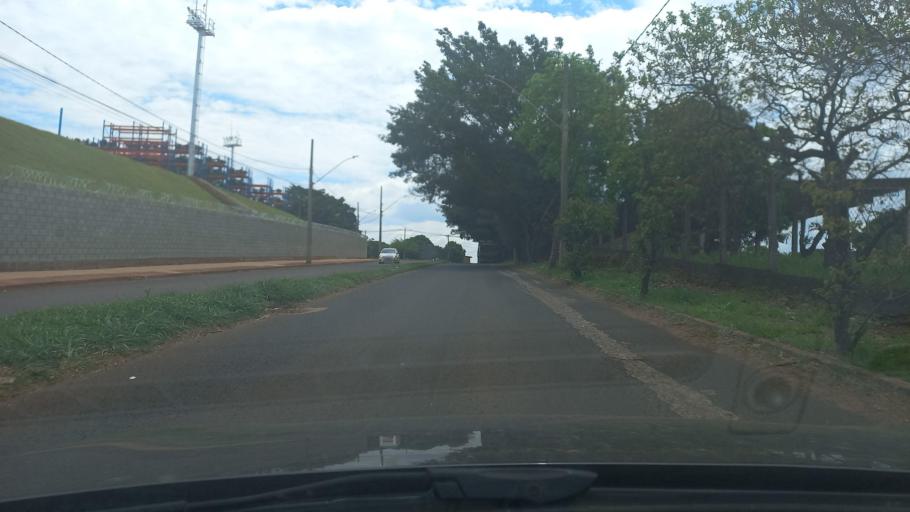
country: BR
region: Minas Gerais
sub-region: Uberaba
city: Uberaba
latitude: -19.7343
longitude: -47.9761
